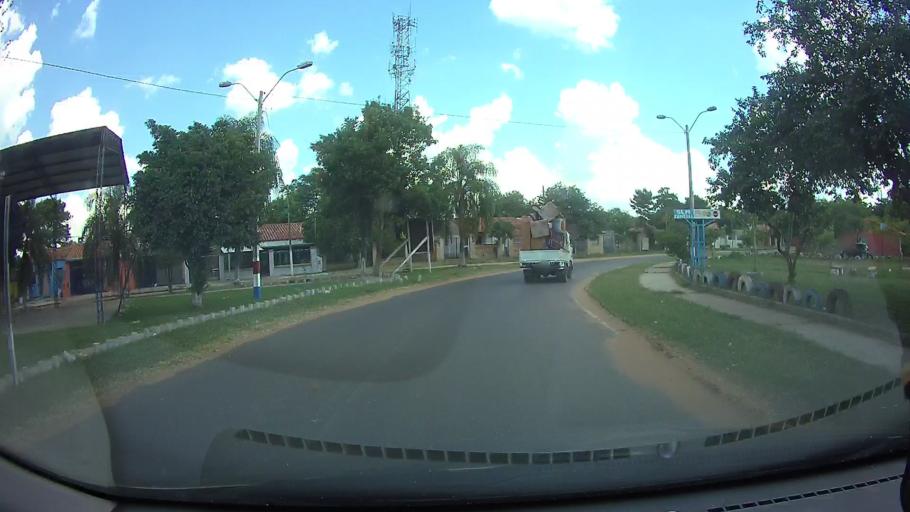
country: PY
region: Central
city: Limpio
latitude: -25.1667
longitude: -57.4344
